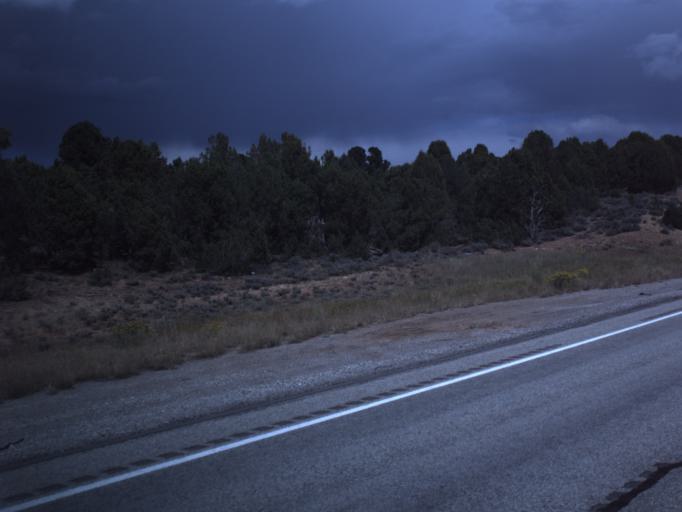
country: US
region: Utah
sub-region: San Juan County
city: Monticello
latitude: 37.7658
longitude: -109.3829
